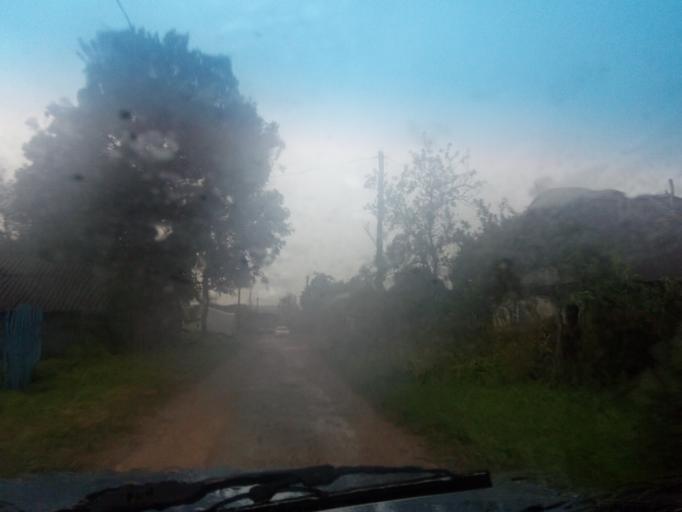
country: BY
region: Vitebsk
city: Dzisna
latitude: 55.6755
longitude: 28.3265
